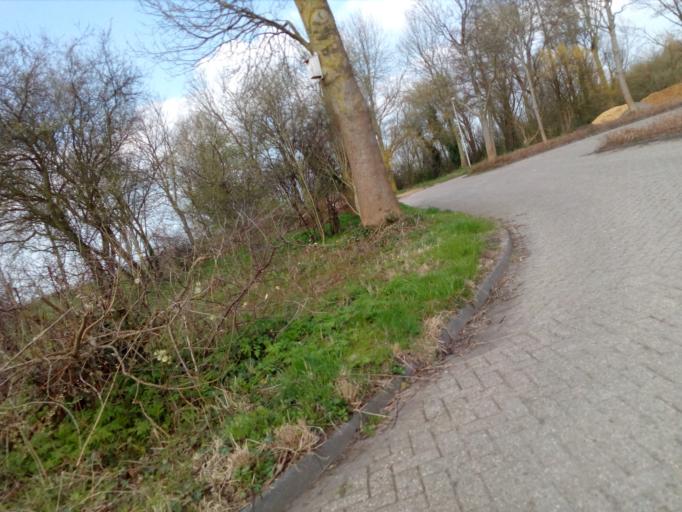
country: NL
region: South Holland
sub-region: Gemeente Zoetermeer
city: Zoetermeer
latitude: 52.0783
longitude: 4.4981
